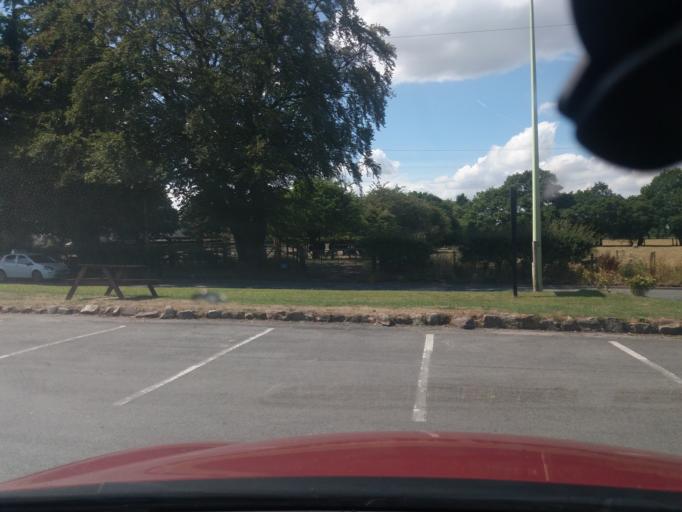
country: GB
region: England
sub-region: Lancashire
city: Euxton
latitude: 53.6762
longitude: -2.6775
